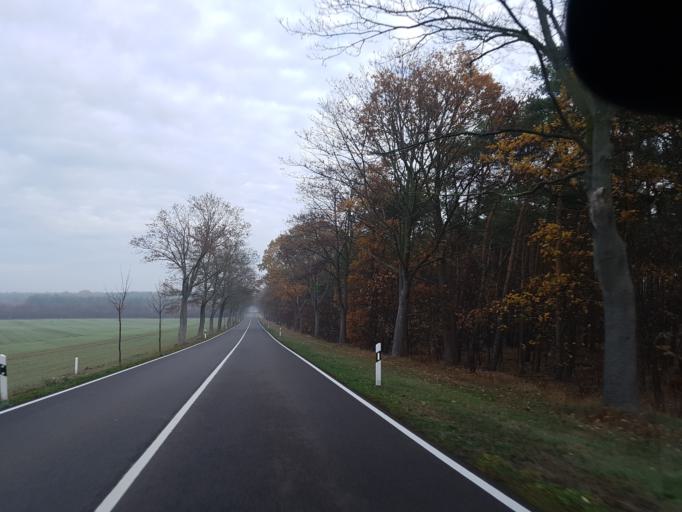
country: DE
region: Saxony-Anhalt
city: Kropstadt
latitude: 51.9759
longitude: 12.7592
